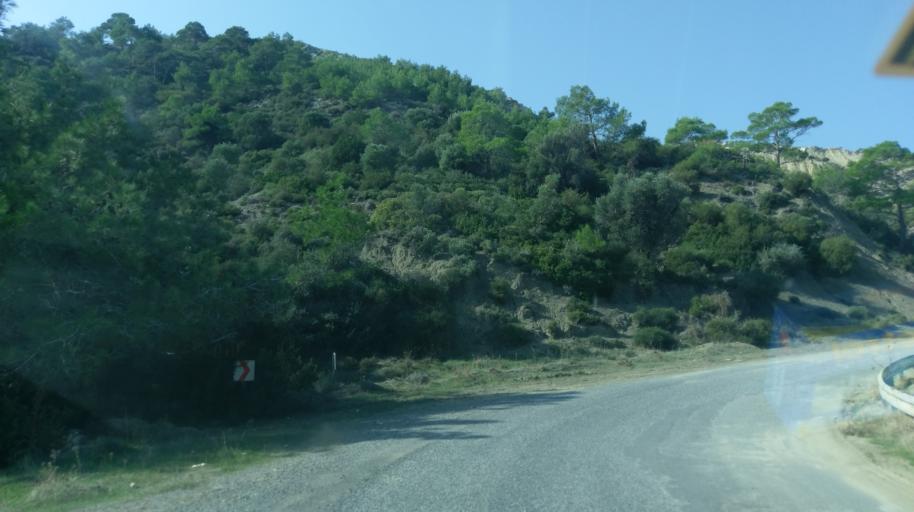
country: CY
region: Keryneia
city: Lapithos
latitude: 35.3516
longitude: 33.0727
